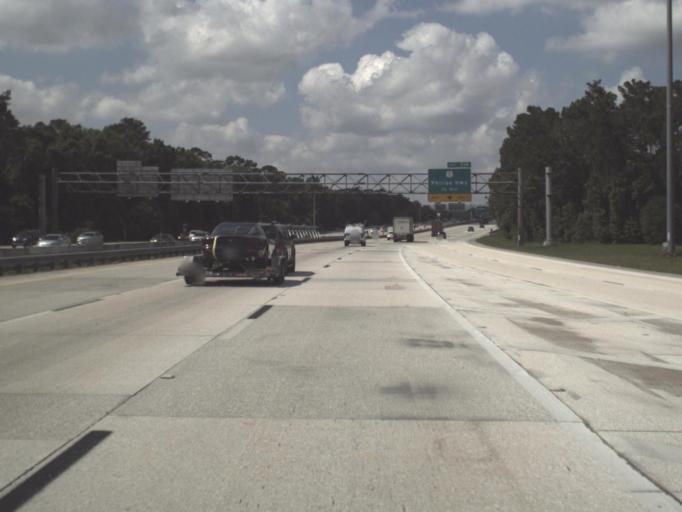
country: US
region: Florida
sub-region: Saint Johns County
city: Fruit Cove
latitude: 30.1768
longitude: -81.5588
